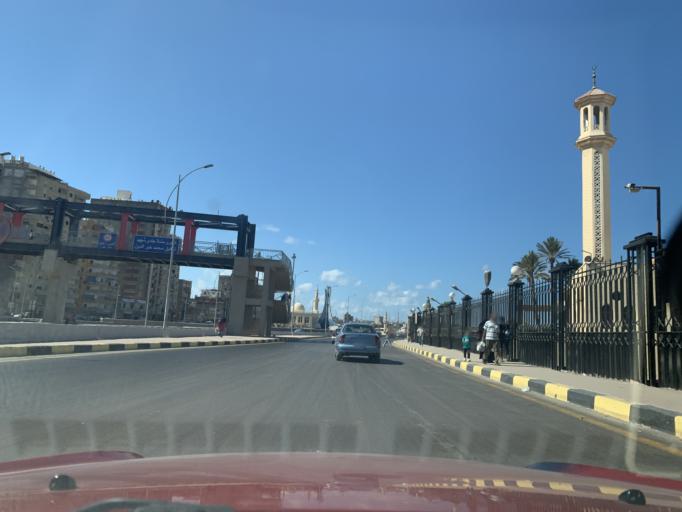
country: EG
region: Alexandria
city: Alexandria
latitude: 31.2205
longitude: 29.9908
